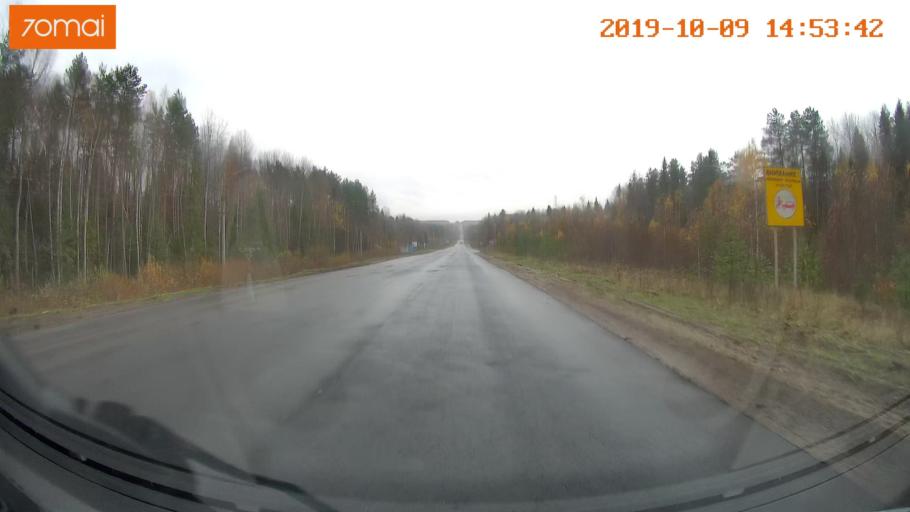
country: RU
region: Kostroma
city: Chistyye Bory
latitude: 58.3646
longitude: 41.6396
